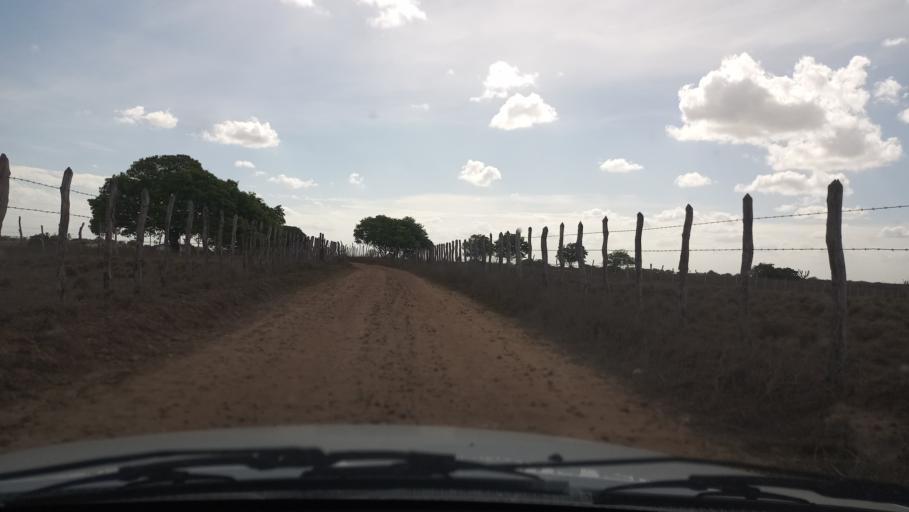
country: BR
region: Rio Grande do Norte
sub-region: Goianinha
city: Goianinha
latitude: -6.3048
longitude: -35.3035
